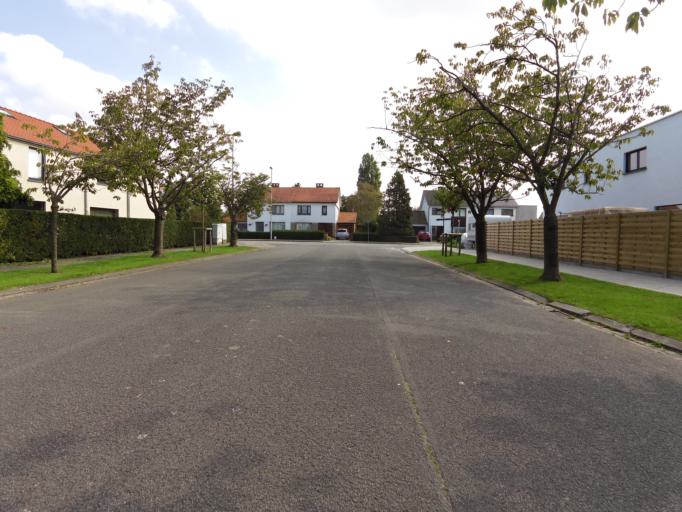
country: BE
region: Flanders
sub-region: Provincie West-Vlaanderen
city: Ostend
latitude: 51.2051
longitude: 2.9125
